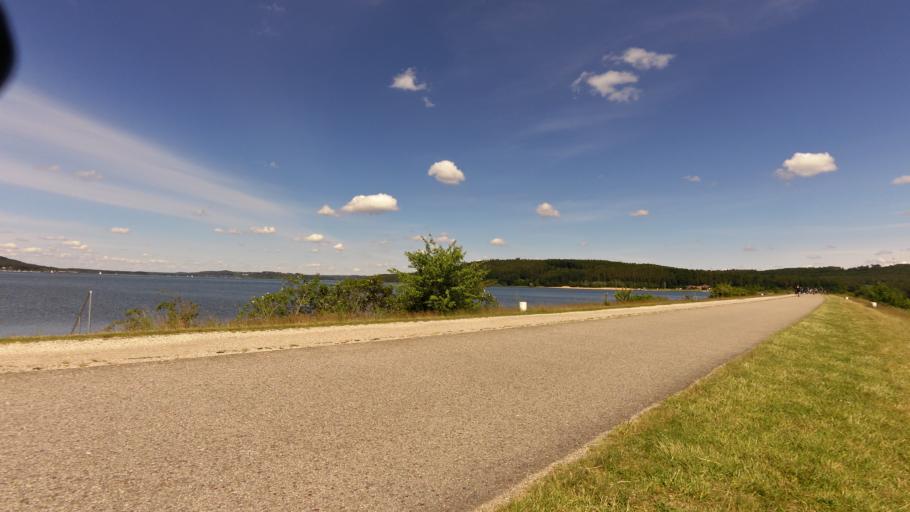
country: DE
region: Bavaria
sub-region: Regierungsbezirk Mittelfranken
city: Pleinfeld
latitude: 49.1252
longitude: 10.9642
